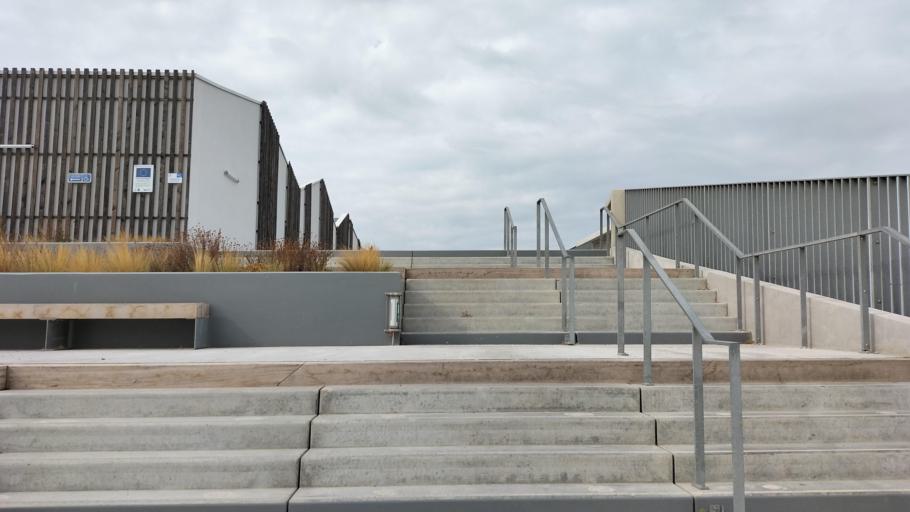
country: FR
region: Poitou-Charentes
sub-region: Departement de la Charente-Maritime
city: Dolus-d'Oleron
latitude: 45.9124
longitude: -1.3246
